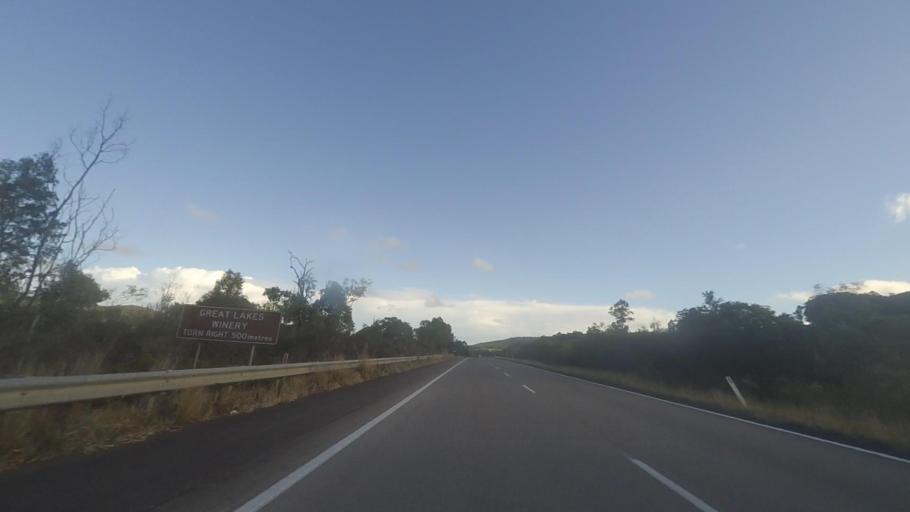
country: AU
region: New South Wales
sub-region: Great Lakes
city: Nabiac
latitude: -32.2567
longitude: 152.3250
